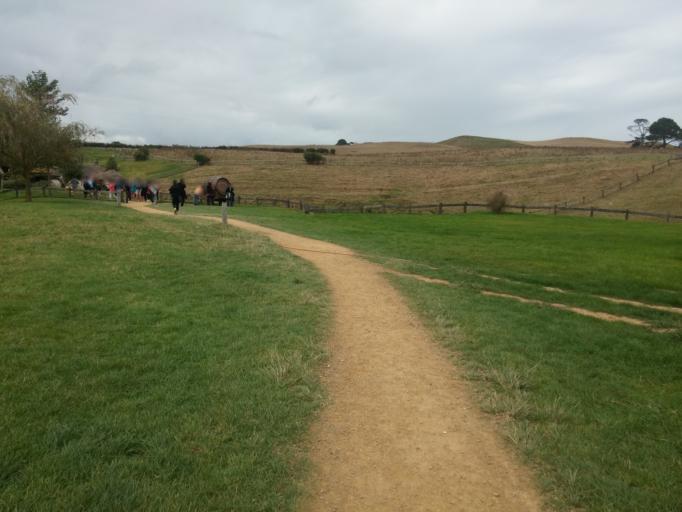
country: NZ
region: Waikato
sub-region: Matamata-Piako District
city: Matamata
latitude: -37.8593
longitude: 175.6799
